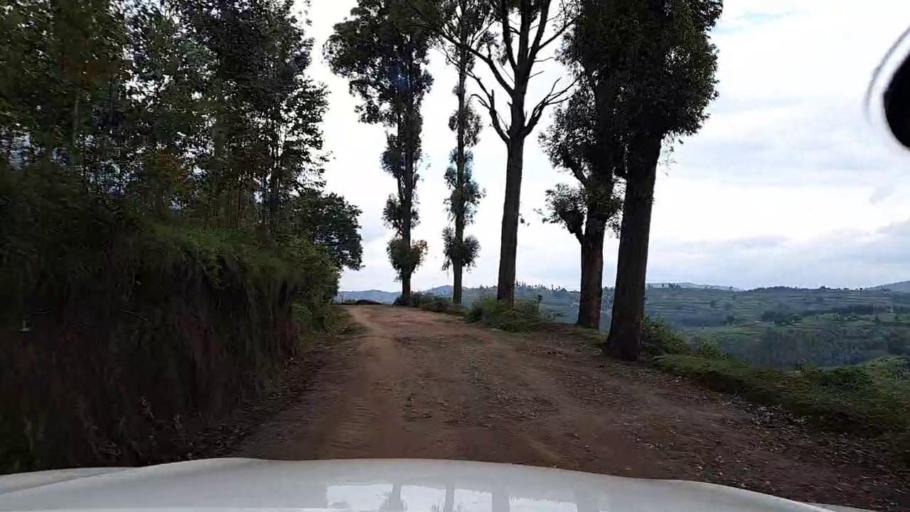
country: BI
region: Kayanza
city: Kayanza
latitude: -2.7947
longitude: 29.5127
